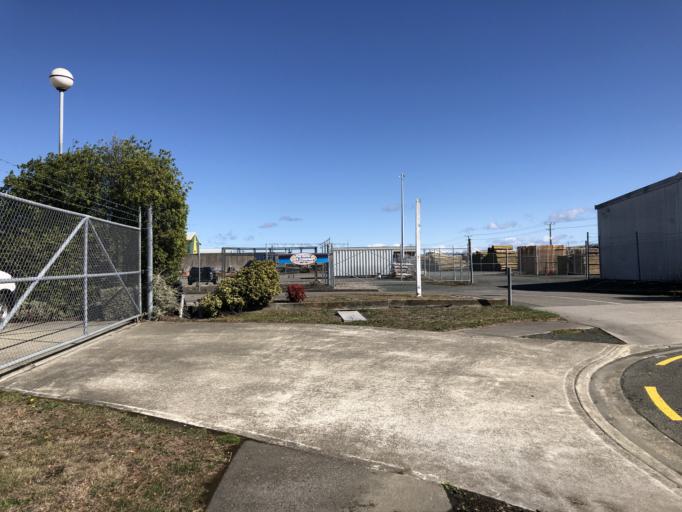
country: NZ
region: Tasman
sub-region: Tasman District
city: Richmond
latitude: -41.3423
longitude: 173.1702
